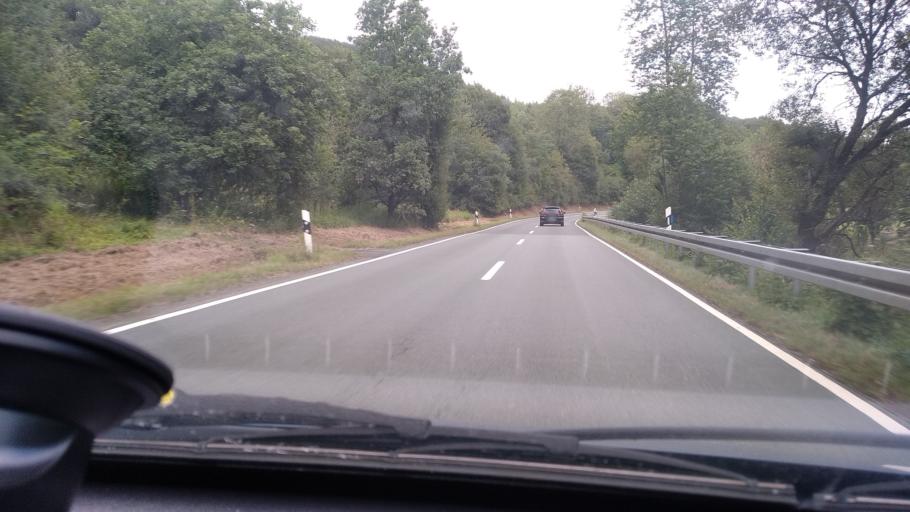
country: DE
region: Hesse
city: Dillenburg
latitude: 50.7769
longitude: 8.3421
